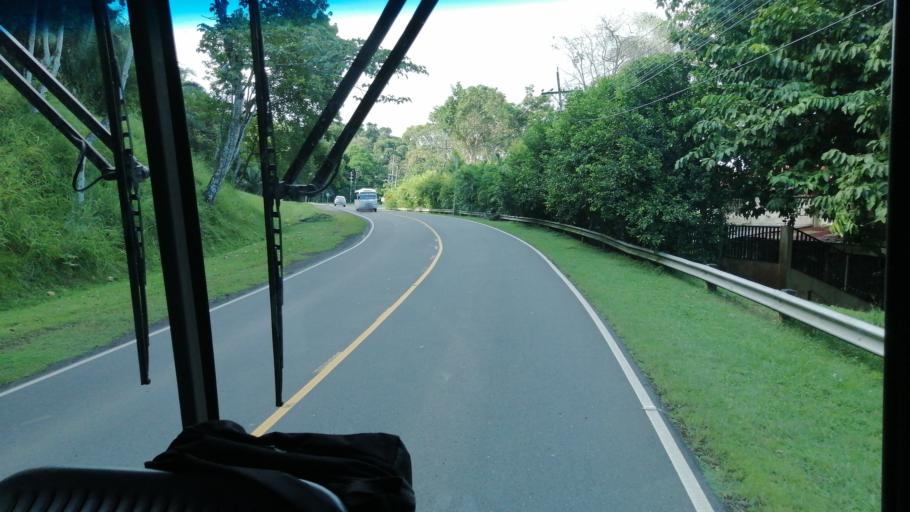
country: PA
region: Panama
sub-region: Distrito de Panama
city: Ancon
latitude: 8.9430
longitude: -79.5913
